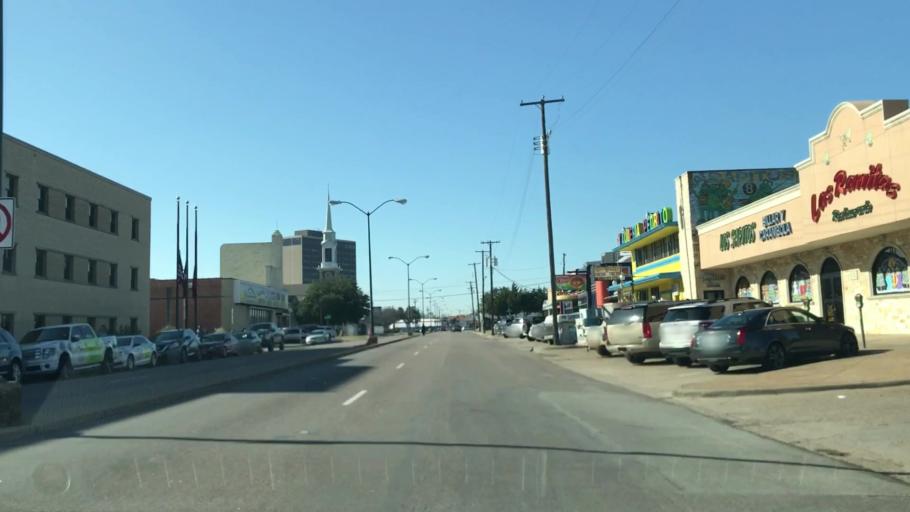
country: US
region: Texas
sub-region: Dallas County
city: Dallas
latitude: 32.7453
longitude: -96.8194
